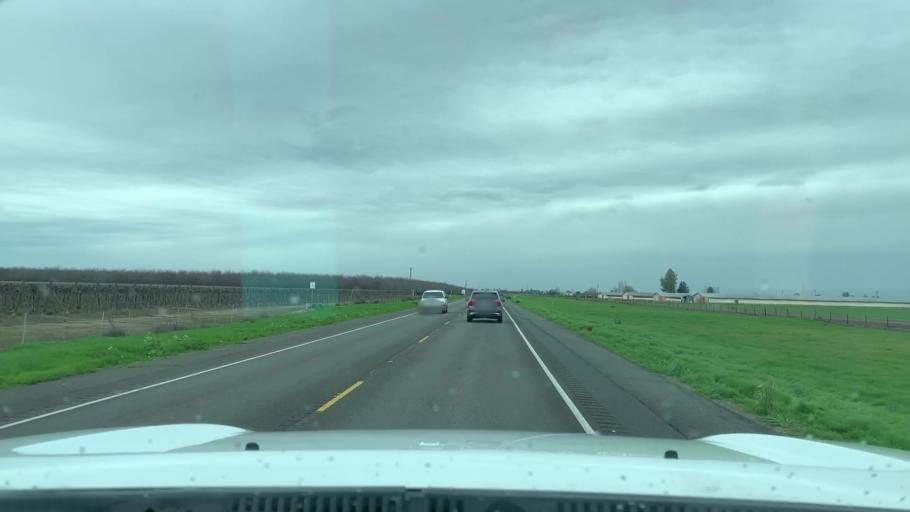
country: US
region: California
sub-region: Fresno County
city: Caruthers
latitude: 36.4759
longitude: -119.7932
